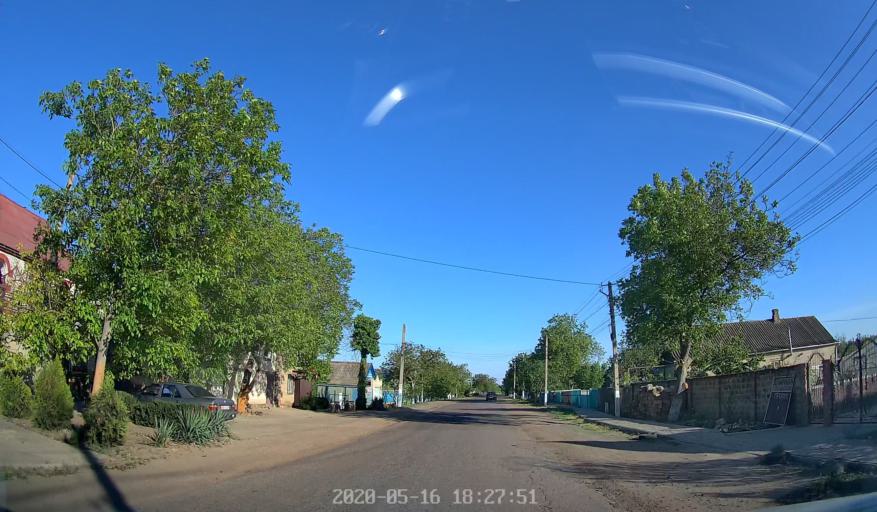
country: MD
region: Telenesti
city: Dnestrovsc
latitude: 46.5446
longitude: 30.0118
